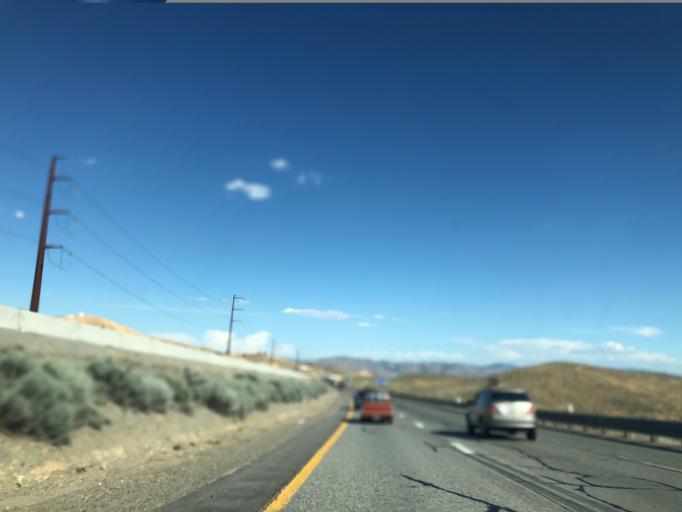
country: US
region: Nevada
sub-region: Washoe County
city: Golden Valley
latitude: 39.5802
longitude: -119.8176
